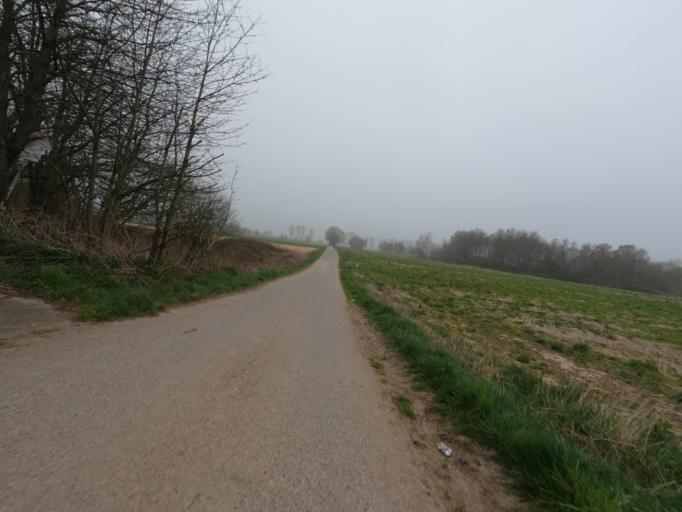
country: NL
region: Limburg
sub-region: Gemeente Roerdalen
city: Vlodrop
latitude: 51.1186
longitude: 6.0950
